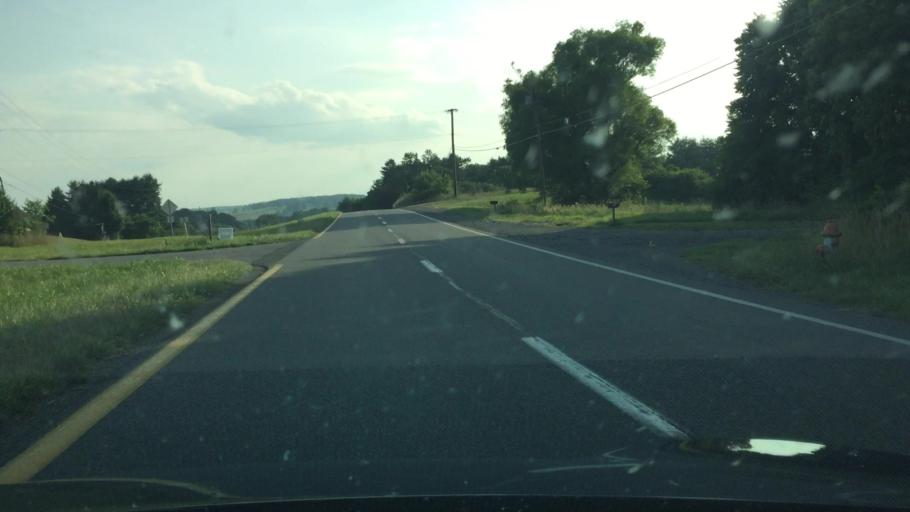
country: US
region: Virginia
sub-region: Pulaski County
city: Fairlawn
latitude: 37.1410
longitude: -80.6056
